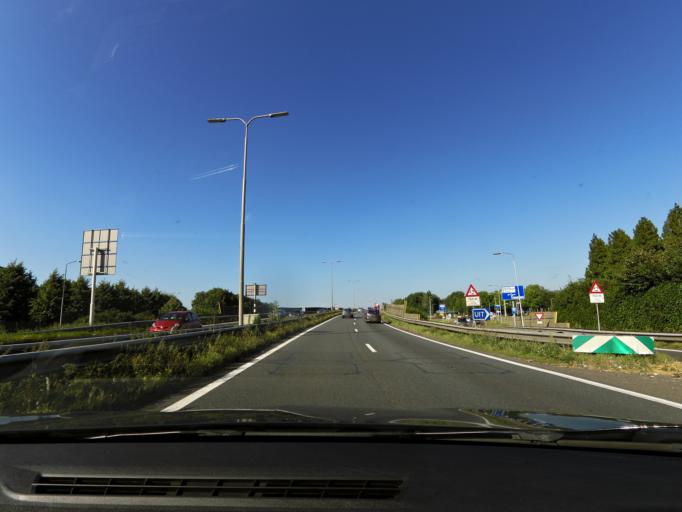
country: NL
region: South Holland
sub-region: Gemeente Papendrecht
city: Papendrecht
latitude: 51.8293
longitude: 4.7054
